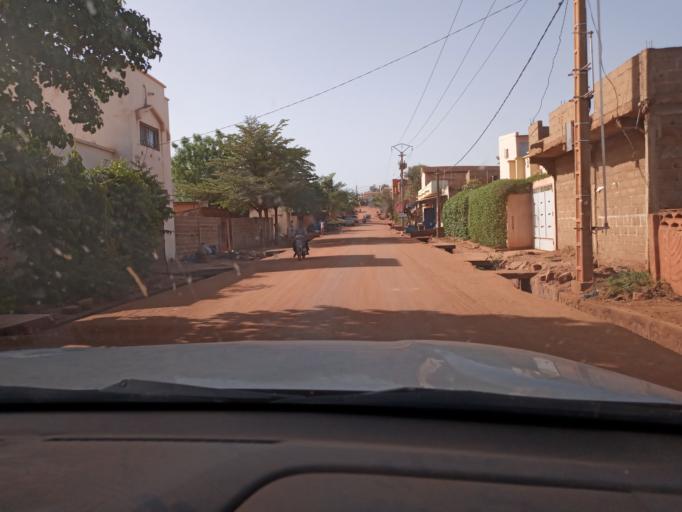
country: ML
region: Bamako
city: Bamako
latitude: 12.6711
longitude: -7.9178
